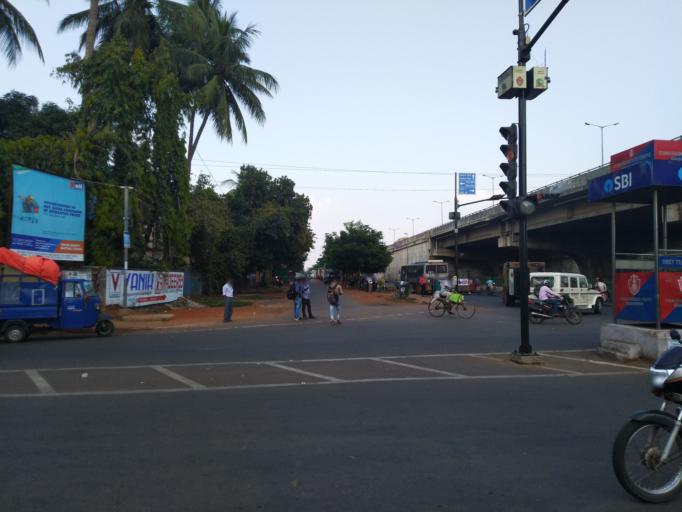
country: IN
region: Odisha
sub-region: Khordha
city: Bhubaneshwar
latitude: 20.2852
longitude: 85.8076
